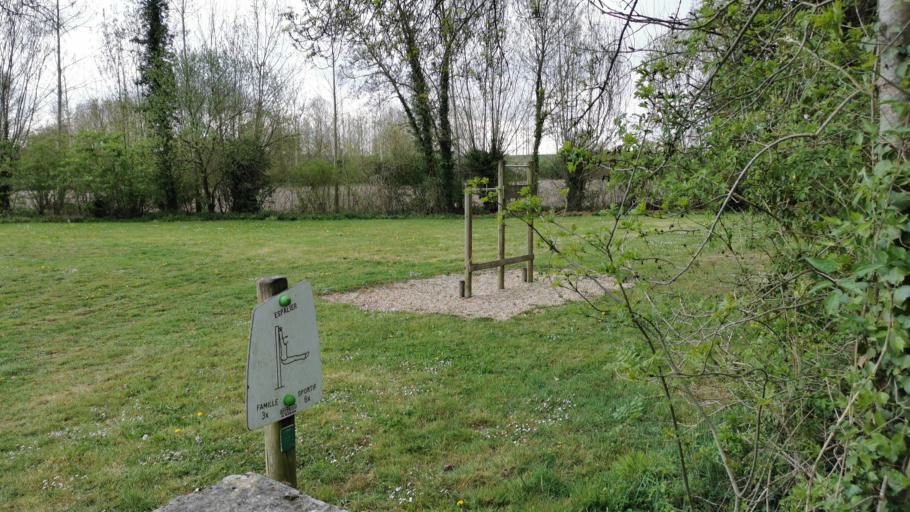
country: FR
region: Poitou-Charentes
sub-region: Departement des Deux-Sevres
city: Mauze-sur-le-Mignon
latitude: 46.1997
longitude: -0.6812
